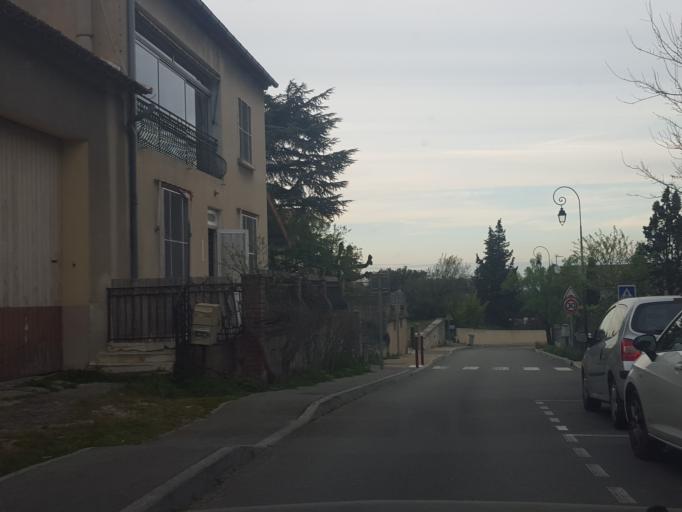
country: FR
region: Provence-Alpes-Cote d'Azur
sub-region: Departement du Vaucluse
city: Chateauneuf-de-Gadagne
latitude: 43.9299
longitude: 4.9460
